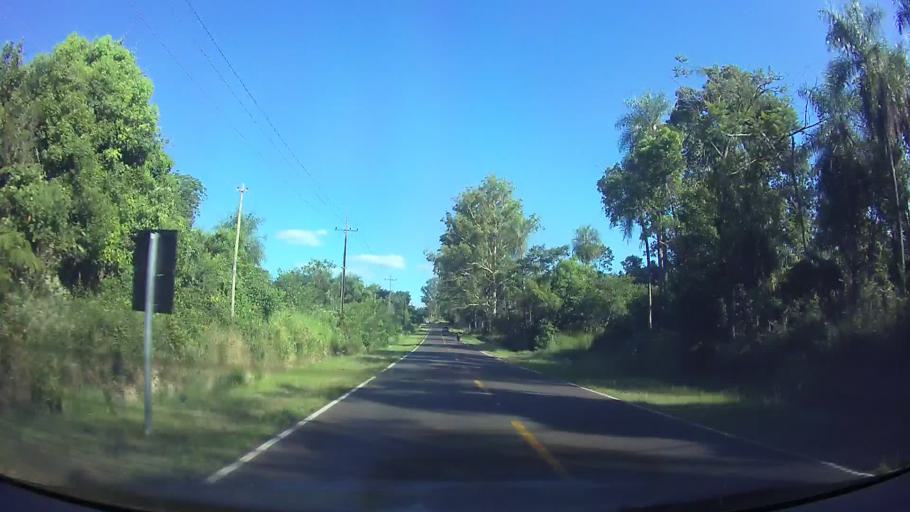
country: PY
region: Cordillera
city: Atyra
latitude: -25.3070
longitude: -57.1553
